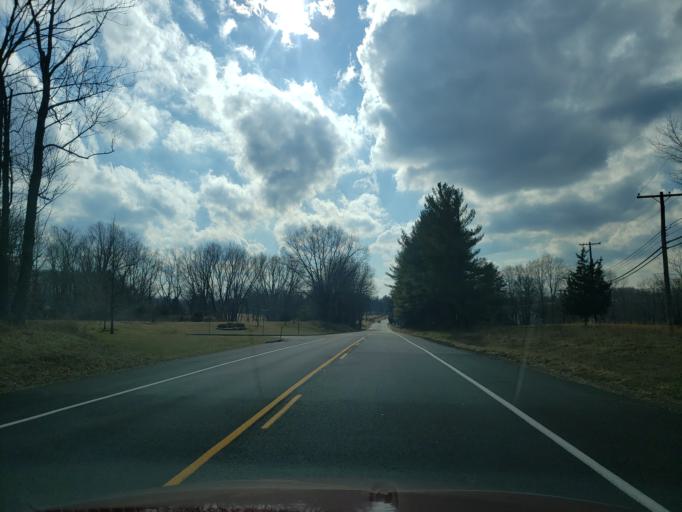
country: US
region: New Jersey
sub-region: Hunterdon County
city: Lambertville
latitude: 40.4404
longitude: -74.9476
